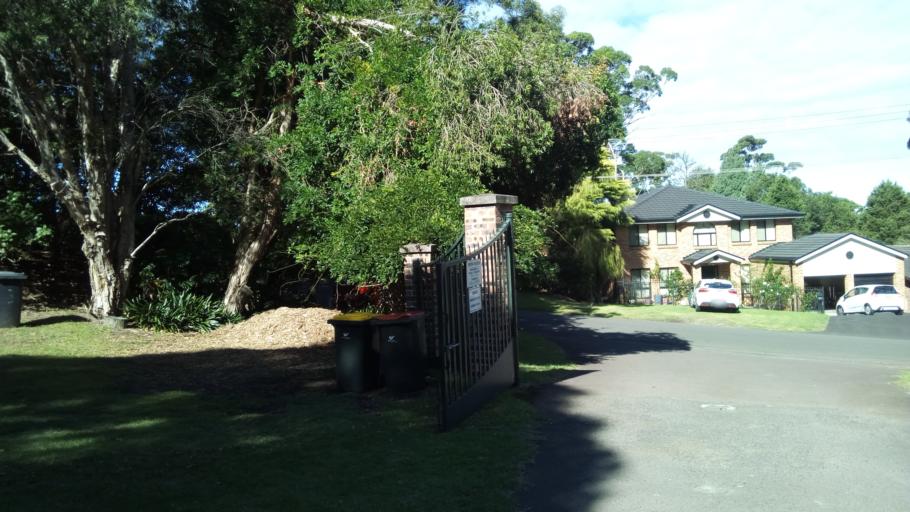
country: AU
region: New South Wales
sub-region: Wollongong
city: Mount Ousley
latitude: -34.3968
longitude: 150.8602
